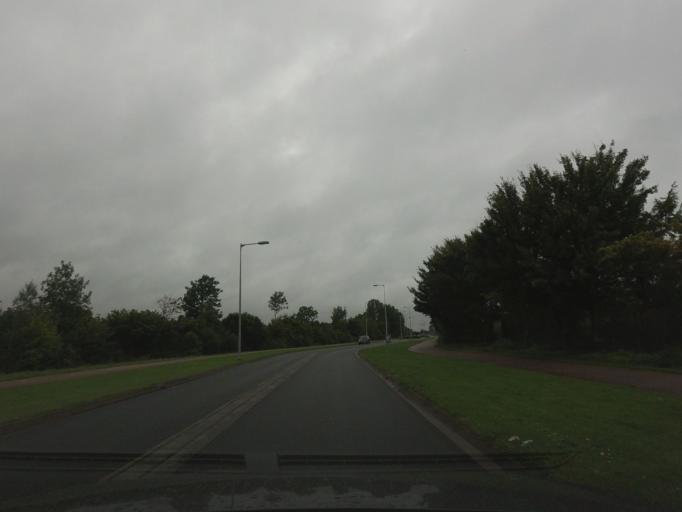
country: NL
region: North Holland
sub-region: Gemeente Haarlemmermeer
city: Hoofddorp
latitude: 52.3079
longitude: 4.6536
